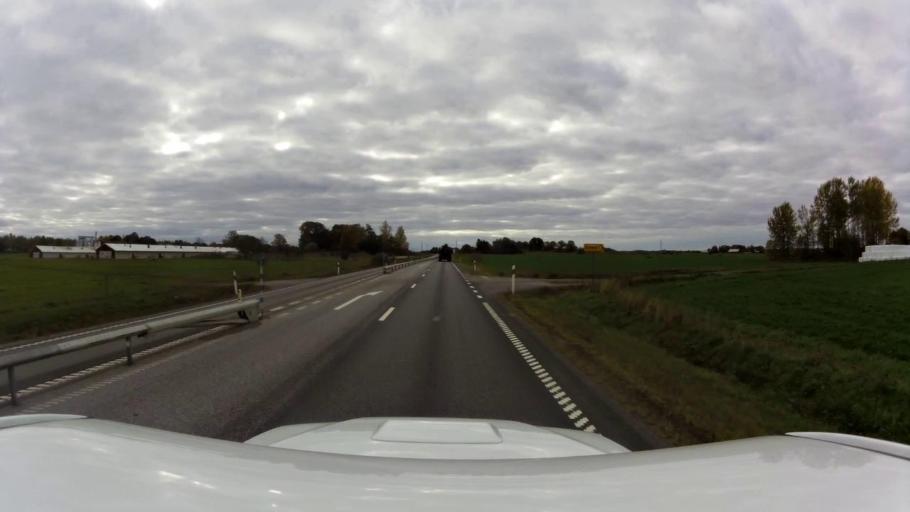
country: SE
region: OEstergoetland
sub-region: Linkopings Kommun
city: Malmslatt
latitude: 58.3455
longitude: 15.5518
